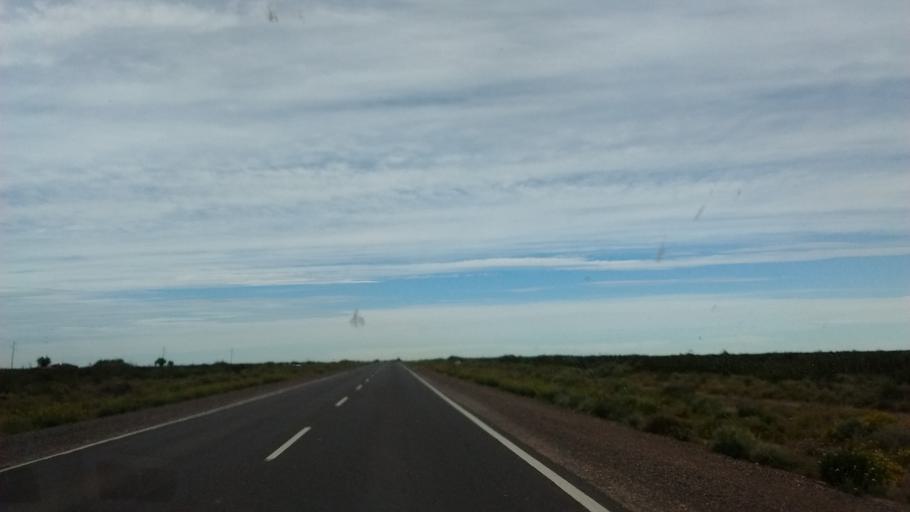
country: AR
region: Rio Negro
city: Contraalmirante Cordero
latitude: -38.5866
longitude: -68.1034
